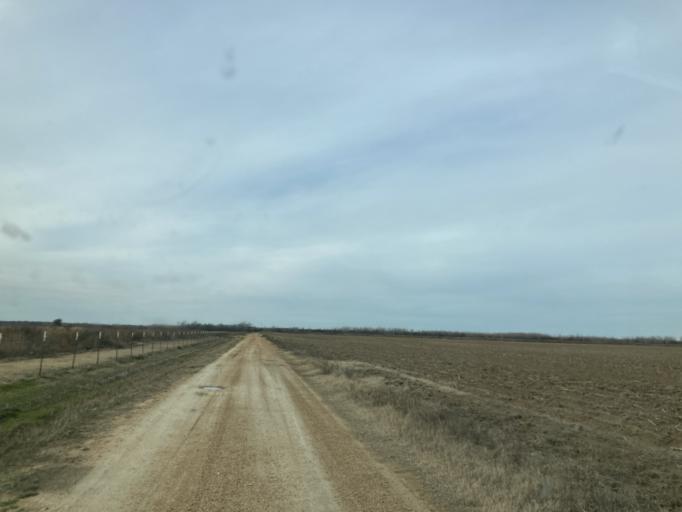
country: US
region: Mississippi
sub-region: Humphreys County
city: Belzoni
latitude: 33.1236
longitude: -90.6181
